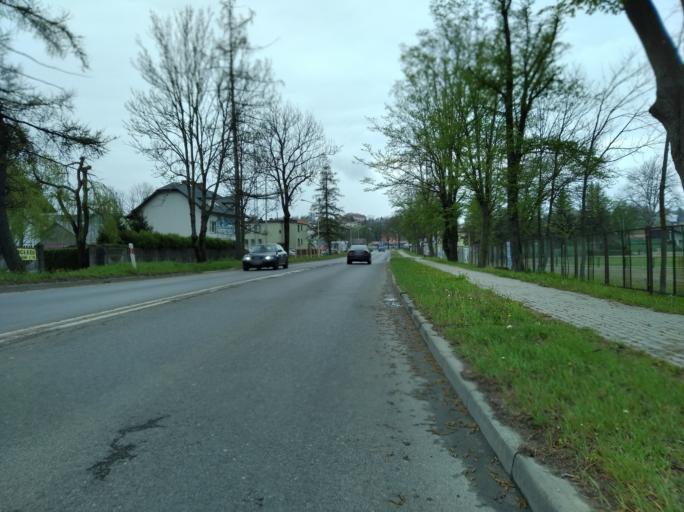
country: PL
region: Subcarpathian Voivodeship
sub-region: Powiat brzozowski
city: Brzozow
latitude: 49.7027
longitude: 22.0213
